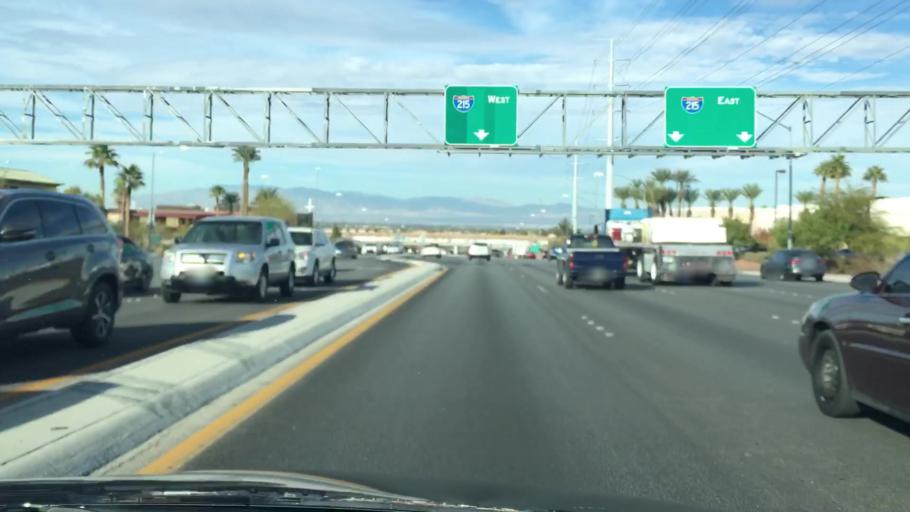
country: US
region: Nevada
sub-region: Clark County
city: Whitney
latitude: 36.0191
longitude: -115.1006
